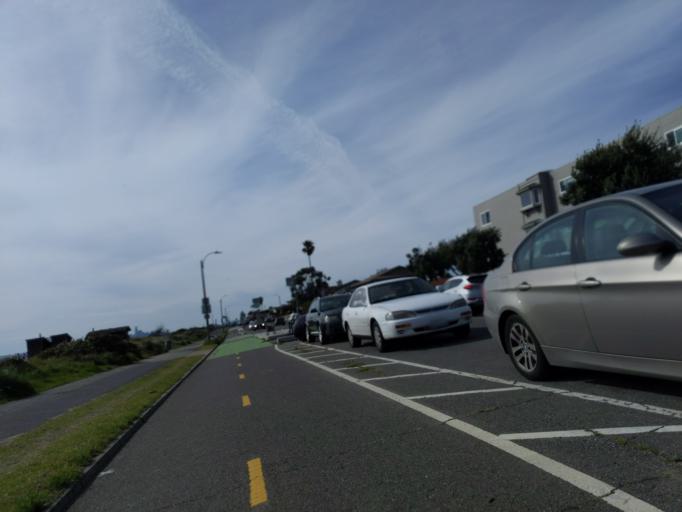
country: US
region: California
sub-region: Alameda County
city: Alameda
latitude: 37.7592
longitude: -122.2635
